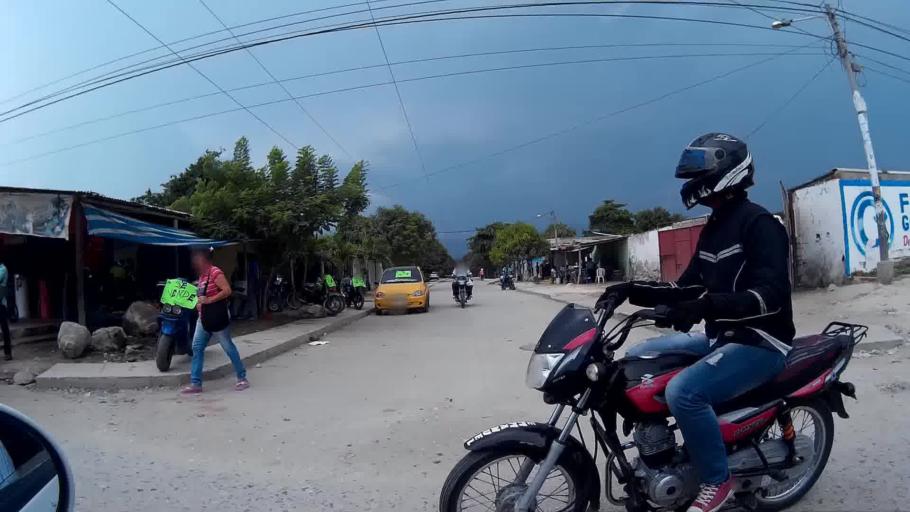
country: CO
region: Magdalena
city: Cienaga
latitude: 11.0068
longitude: -74.2441
